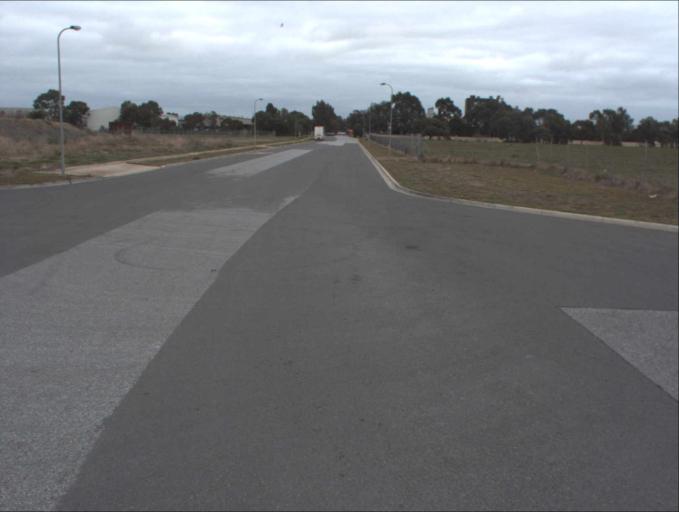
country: AU
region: South Australia
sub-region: Port Adelaide Enfield
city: Blair Athol
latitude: -34.8444
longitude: 138.5768
